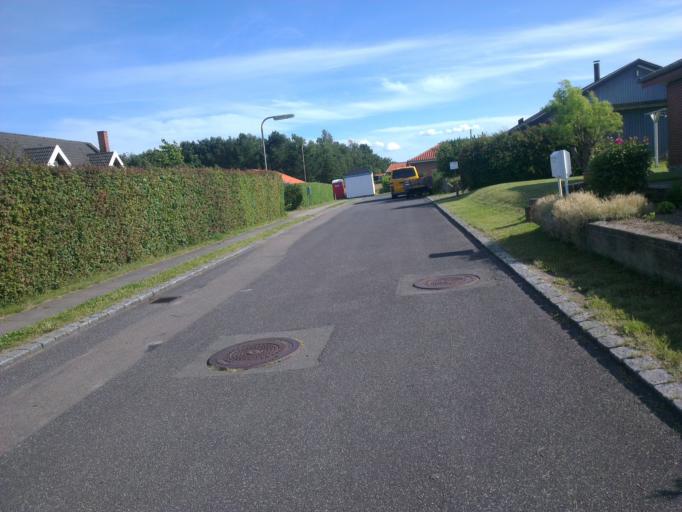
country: DK
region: Capital Region
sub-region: Frederikssund Kommune
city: Skibby
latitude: 55.7443
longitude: 11.9721
